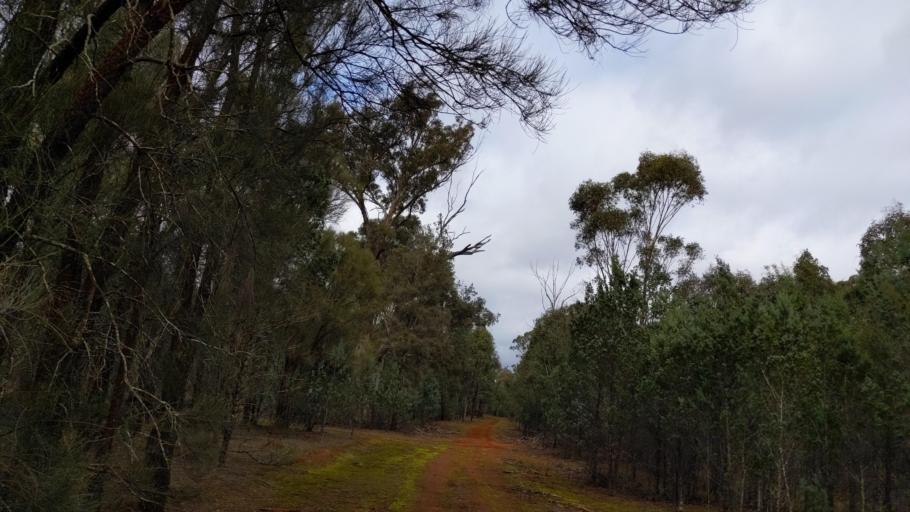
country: AU
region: New South Wales
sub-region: Coolamon
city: Coolamon
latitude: -34.8290
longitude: 146.9357
